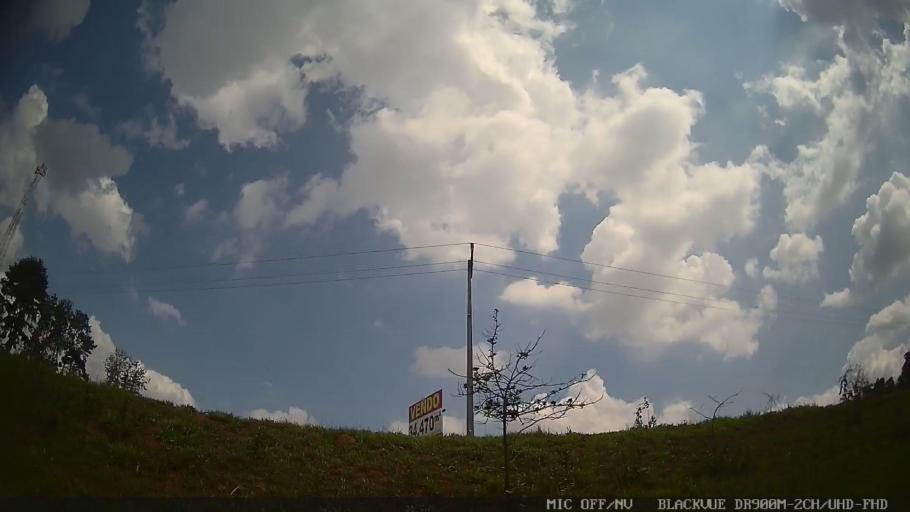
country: BR
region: Sao Paulo
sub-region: Braganca Paulista
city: Braganca Paulista
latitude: -22.9438
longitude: -46.6624
